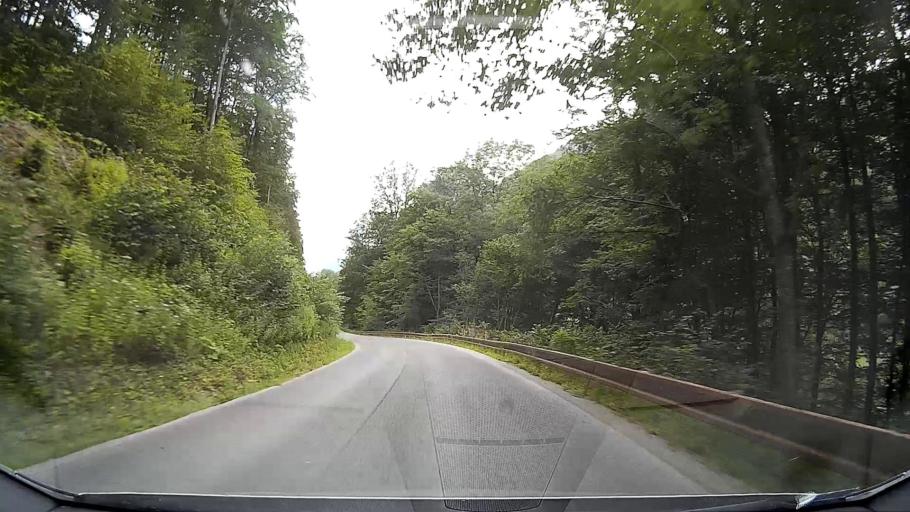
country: SK
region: Banskobystricky
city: Revuca
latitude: 48.7604
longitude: 20.0793
